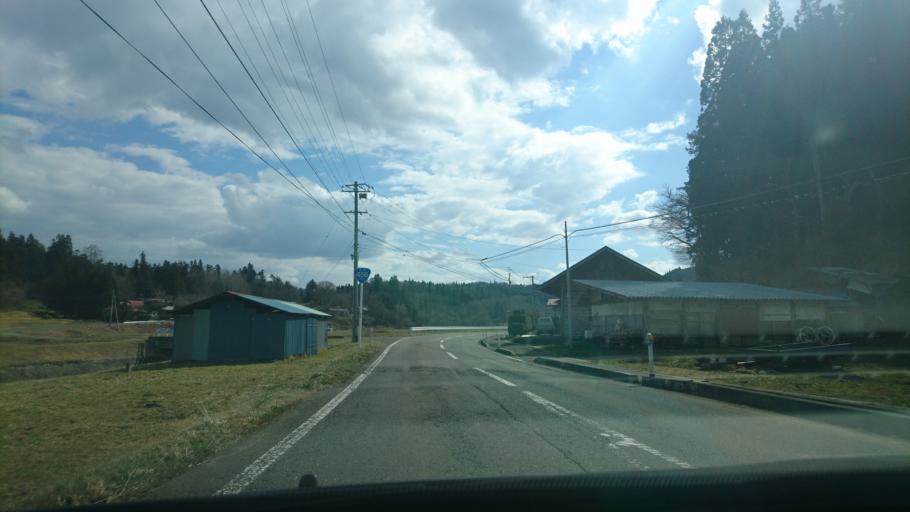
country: JP
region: Iwate
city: Hanamaki
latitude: 39.3452
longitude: 141.2392
